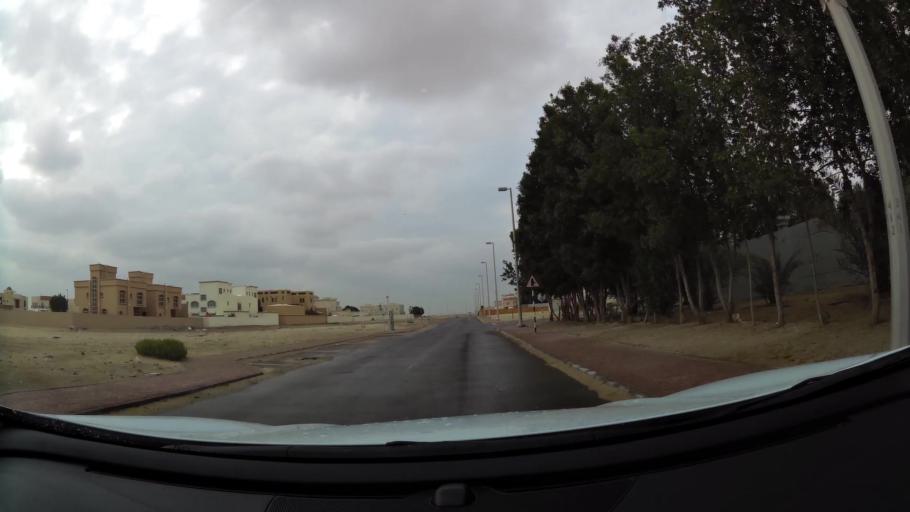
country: AE
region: Abu Dhabi
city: Abu Dhabi
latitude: 24.3567
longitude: 54.6188
